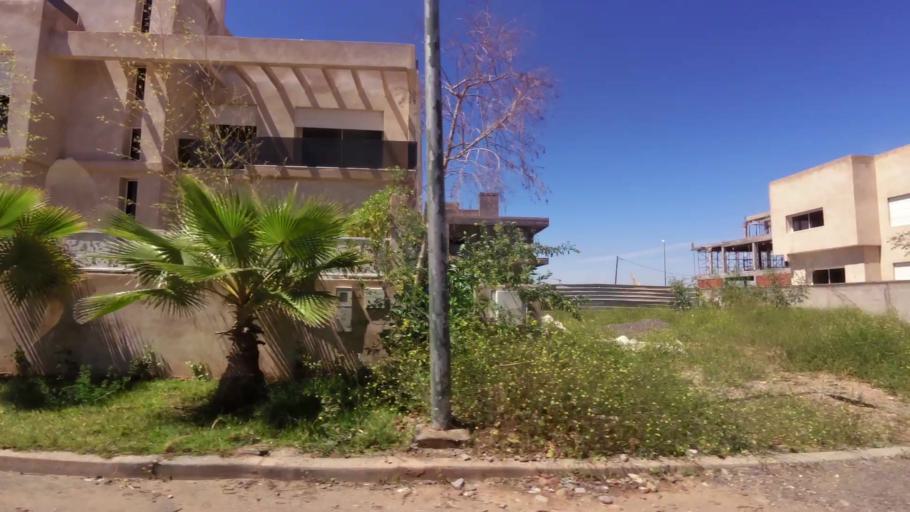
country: MA
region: Marrakech-Tensift-Al Haouz
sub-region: Marrakech
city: Marrakesh
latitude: 31.5805
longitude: -7.9890
